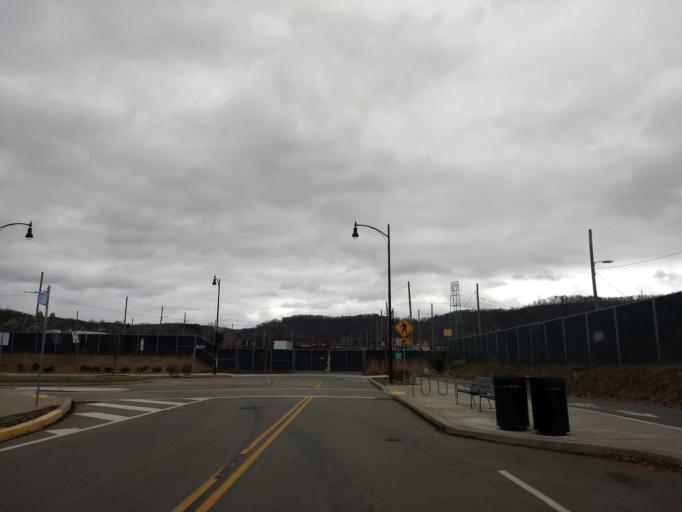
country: US
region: Pennsylvania
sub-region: Allegheny County
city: Homestead
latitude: 40.4110
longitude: -79.9482
